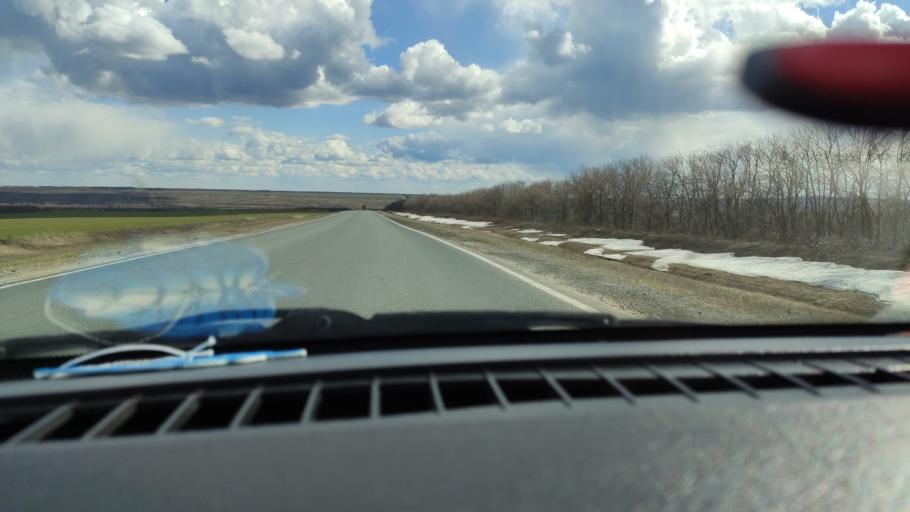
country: RU
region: Saratov
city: Dukhovnitskoye
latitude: 52.7616
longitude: 48.2413
